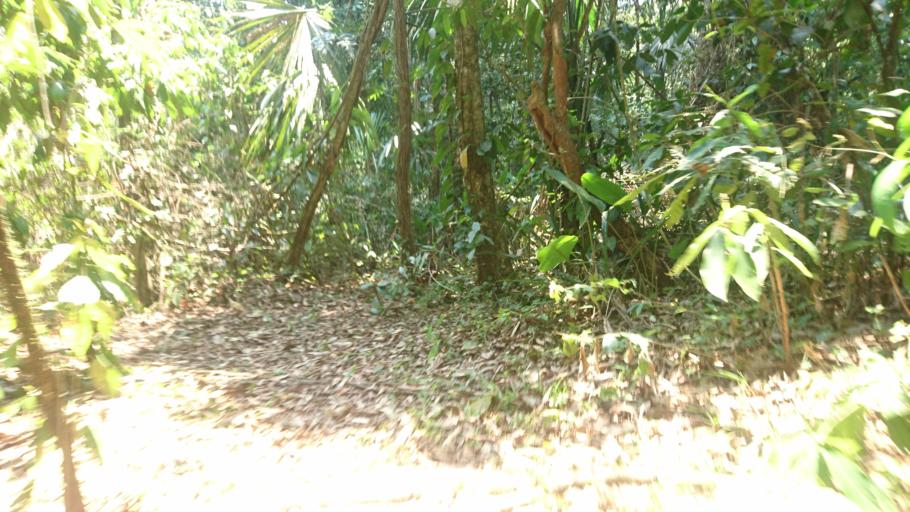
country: MX
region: Chiapas
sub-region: Marques de Comillas
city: Zamora Pico de Oro
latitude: 16.2477
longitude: -90.8304
